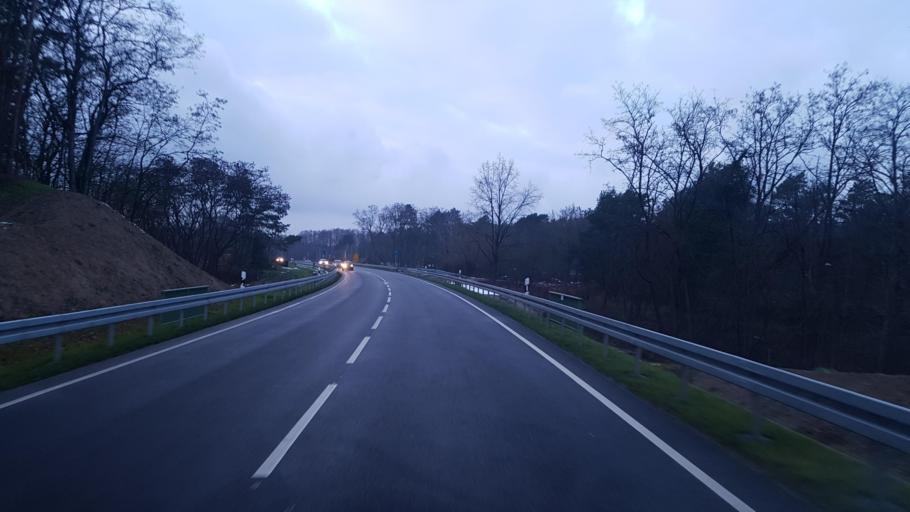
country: DE
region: Brandenburg
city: Wildau
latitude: 52.3230
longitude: 13.6562
